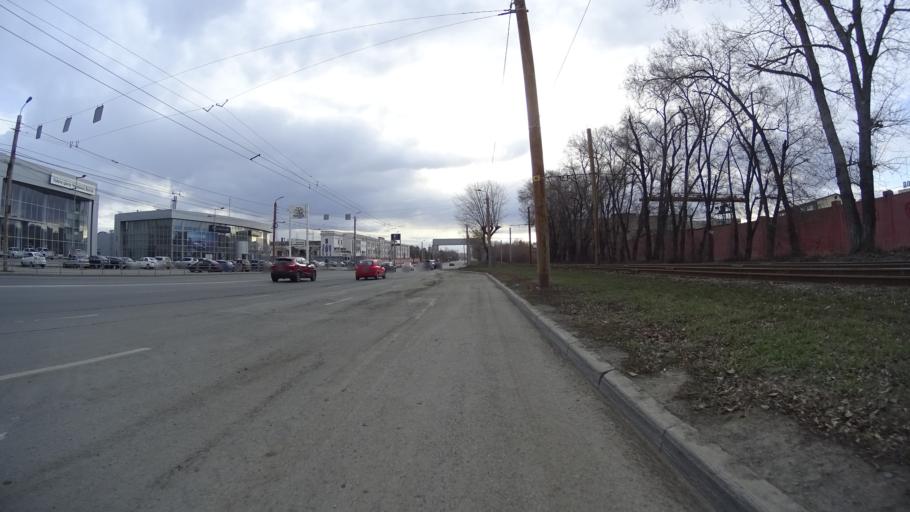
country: RU
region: Chelyabinsk
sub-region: Gorod Chelyabinsk
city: Chelyabinsk
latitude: 55.1594
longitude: 61.4642
